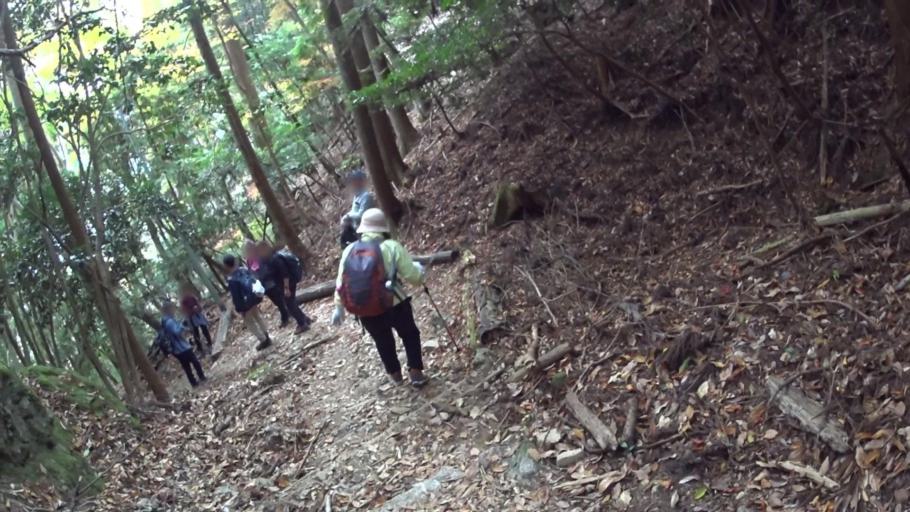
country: JP
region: Kyoto
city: Kameoka
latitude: 35.0566
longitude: 135.6490
